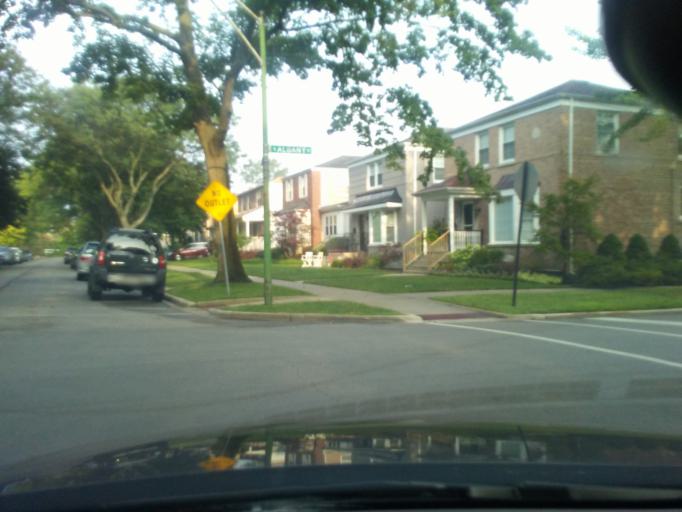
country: US
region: Illinois
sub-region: Cook County
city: Lincolnwood
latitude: 42.0146
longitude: -87.7068
